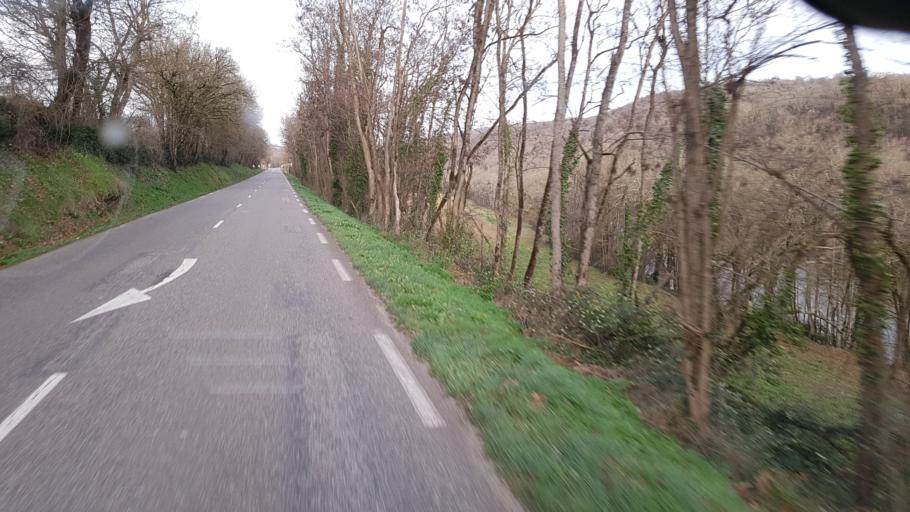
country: FR
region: Midi-Pyrenees
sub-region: Departement du Tarn-et-Garonne
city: Montricoux
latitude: 44.0679
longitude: 1.6549
